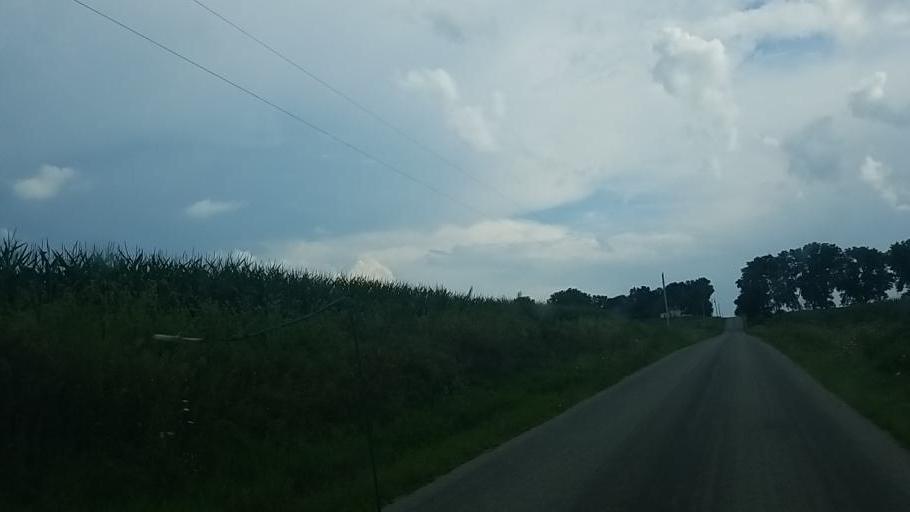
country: US
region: Ohio
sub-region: Medina County
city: Westfield Center
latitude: 40.9836
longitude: -81.9387
